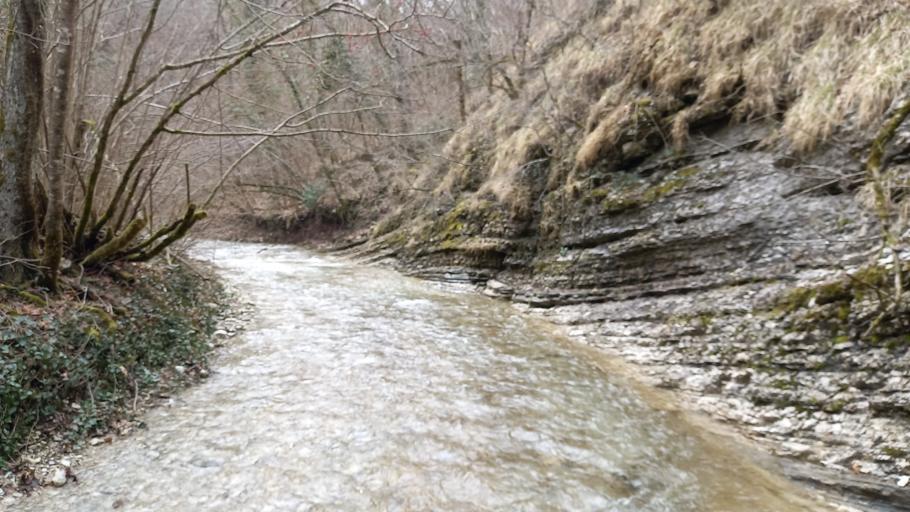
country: RU
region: Krasnodarskiy
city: Dzhubga
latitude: 44.3999
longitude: 38.6977
